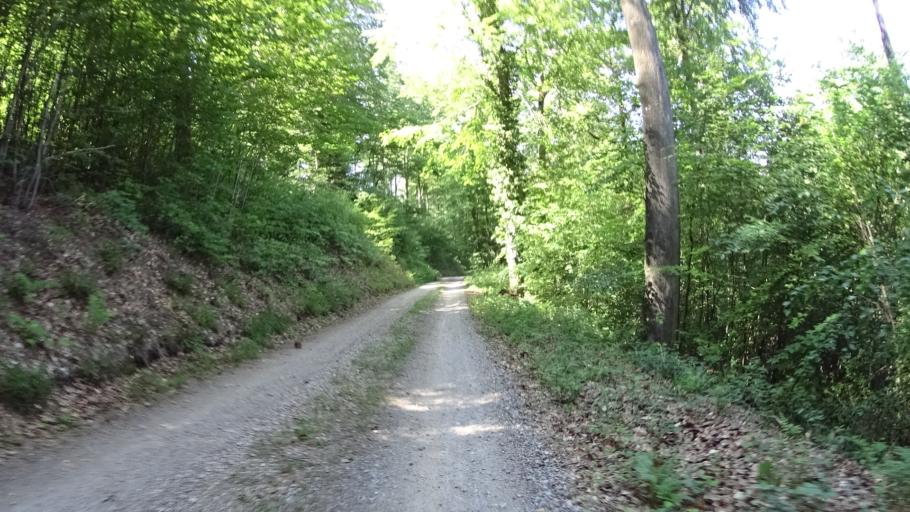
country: DE
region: Baden-Wuerttemberg
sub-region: Karlsruhe Region
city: Dossenheim
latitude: 49.4652
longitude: 8.7079
